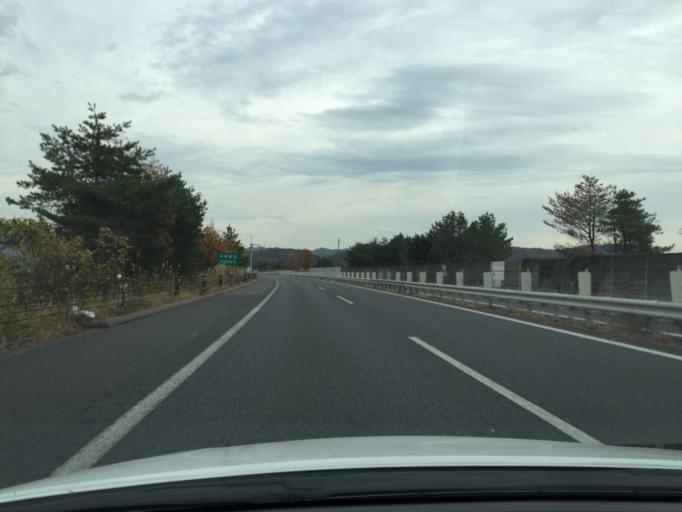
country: JP
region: Fukushima
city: Fukushima-shi
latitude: 37.7181
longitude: 140.4334
